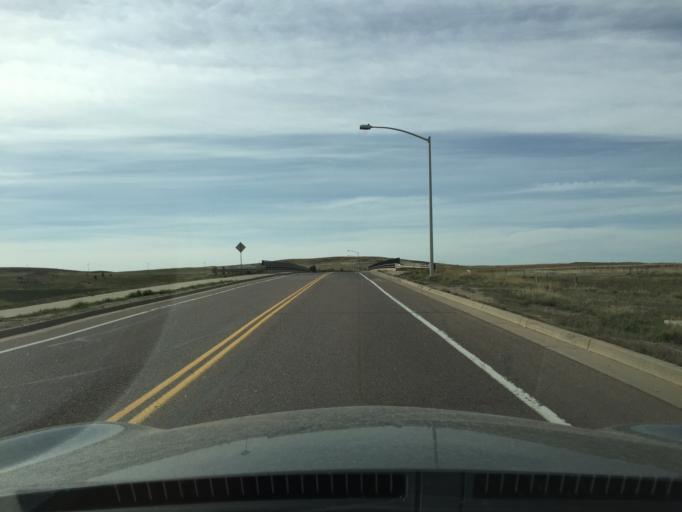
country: US
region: Colorado
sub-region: Boulder County
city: Lafayette
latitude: 39.9826
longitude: -105.0360
